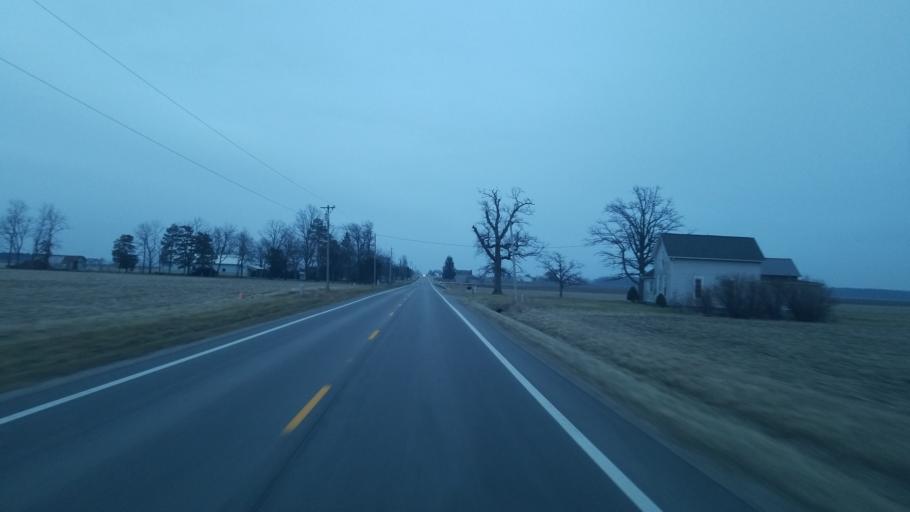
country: US
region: Ohio
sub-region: Mercer County
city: Rockford
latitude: 40.6550
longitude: -84.6605
